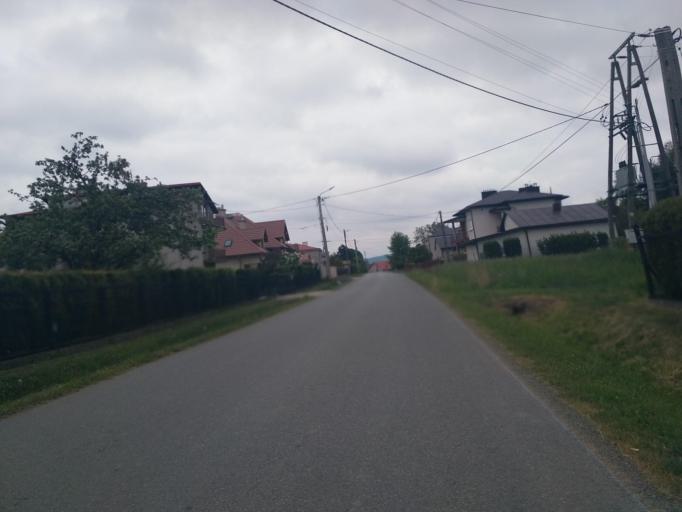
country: PL
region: Subcarpathian Voivodeship
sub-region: Powiat krosnienski
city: Chorkowka
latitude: 49.6674
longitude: 21.7208
